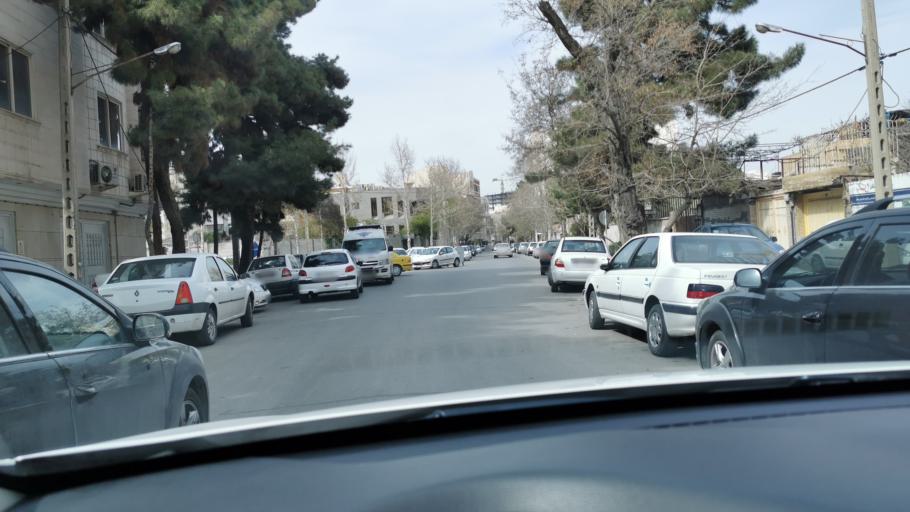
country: IR
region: Razavi Khorasan
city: Mashhad
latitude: 36.2890
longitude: 59.5773
